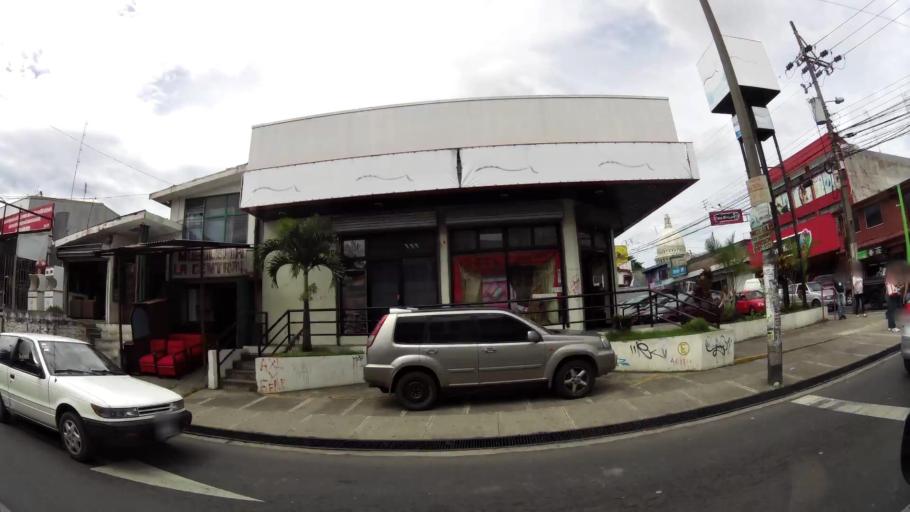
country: CR
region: San Jose
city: San Rafael Arriba
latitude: 9.8967
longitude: -84.0639
